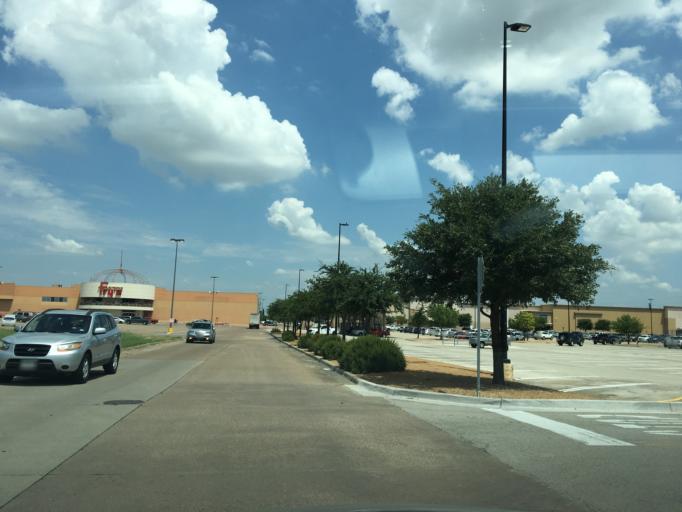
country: US
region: Texas
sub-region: Dallas County
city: Garland
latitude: 32.8657
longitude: -96.6766
